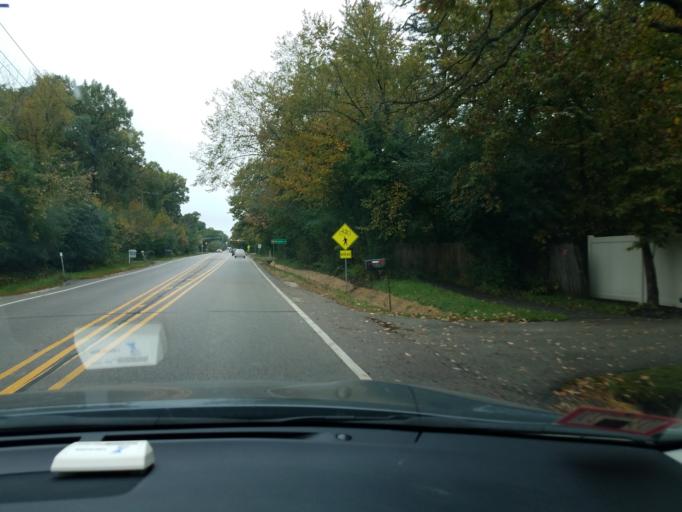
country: US
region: Illinois
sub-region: Lake County
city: Riverwoods
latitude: 42.1675
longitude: -87.8943
